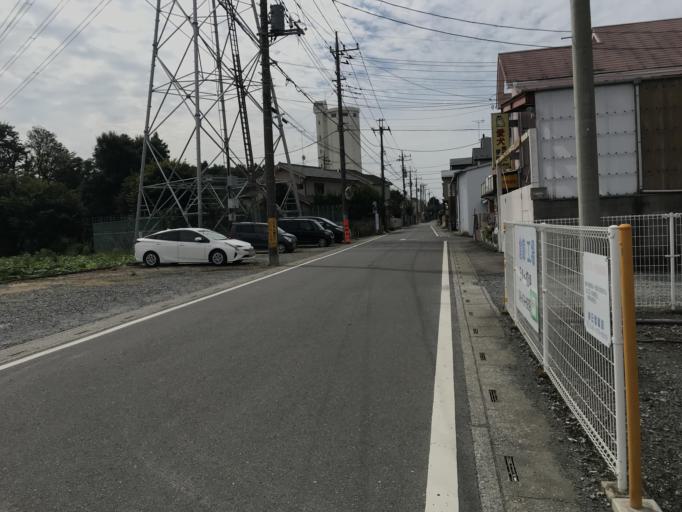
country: JP
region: Saitama
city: Asaka
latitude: 35.7812
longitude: 139.5574
